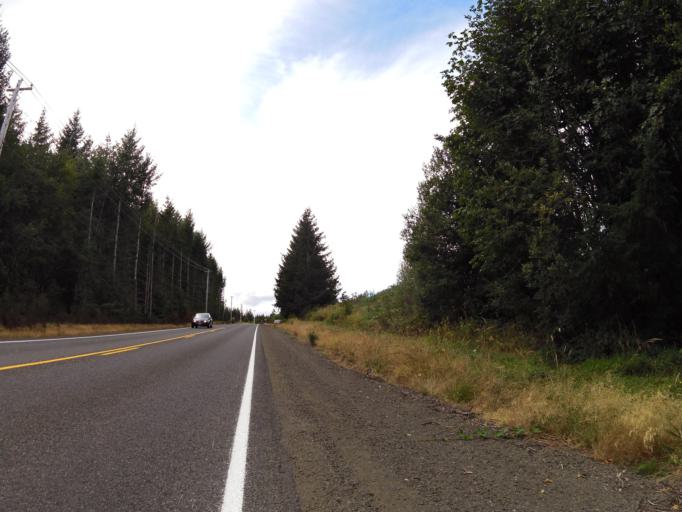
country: US
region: Washington
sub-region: Mason County
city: Shelton
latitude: 47.1490
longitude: -123.0674
